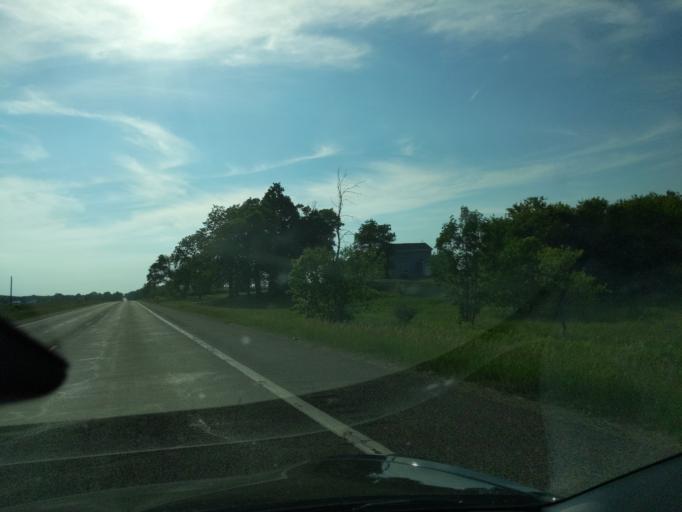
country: US
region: Michigan
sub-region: Barry County
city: Nashville
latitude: 42.6035
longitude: -85.1434
